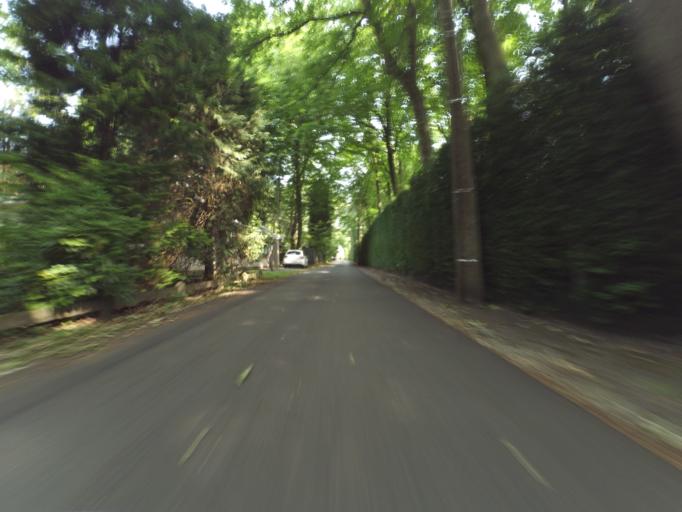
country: BE
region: Flanders
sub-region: Provincie Antwerpen
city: Kalmthout
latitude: 51.3621
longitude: 4.4374
